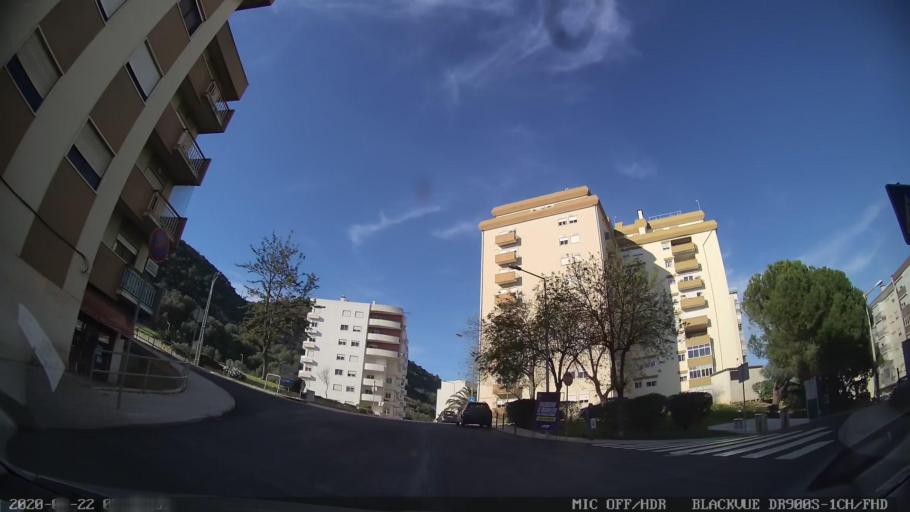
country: PT
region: Lisbon
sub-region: Vila Franca de Xira
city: Vila Franca de Xira
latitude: 38.9609
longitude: -8.9890
